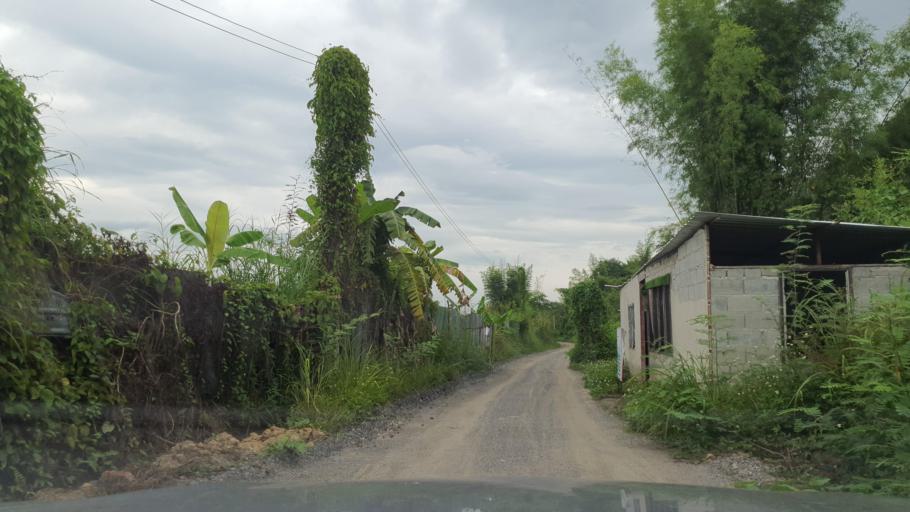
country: TH
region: Chiang Mai
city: San Sai
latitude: 18.9458
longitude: 98.9039
